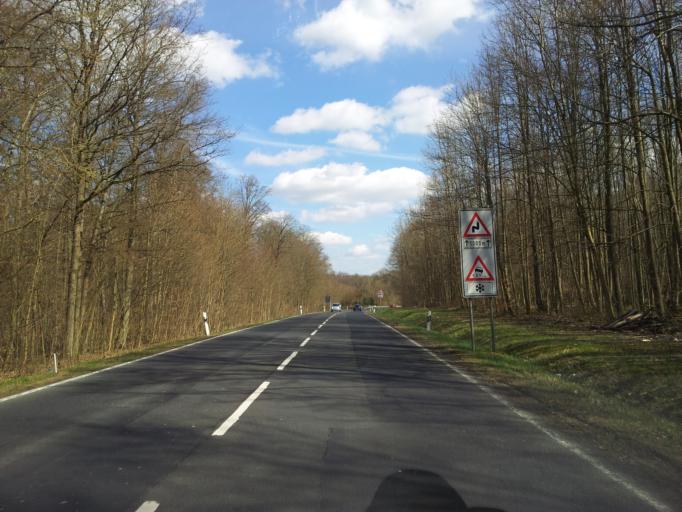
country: DE
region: Bavaria
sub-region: Regierungsbezirk Unterfranken
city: Waldbrunn
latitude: 49.7197
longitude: 9.8022
